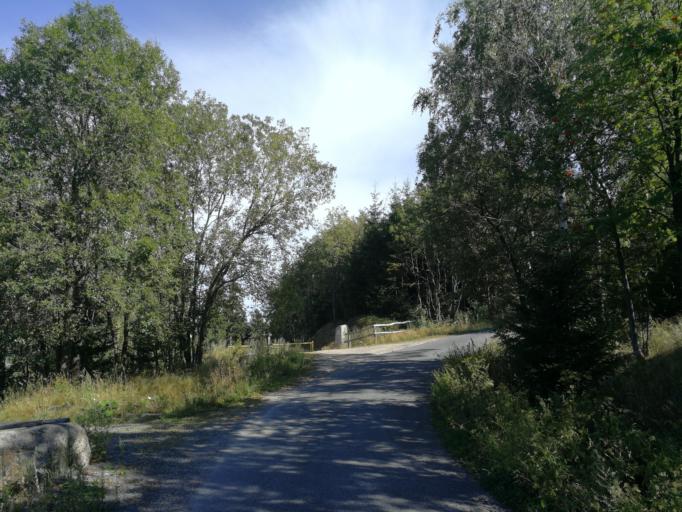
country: CZ
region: Liberecky
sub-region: Okres Jablonec nad Nisou
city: Janov nad Nisou
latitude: 50.7912
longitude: 15.1318
